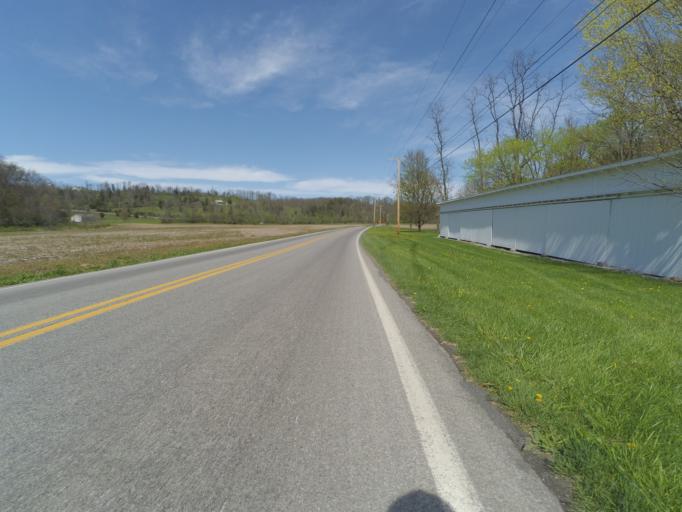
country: US
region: Pennsylvania
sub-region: Blair County
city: Tyrone
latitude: 40.6075
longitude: -78.2021
